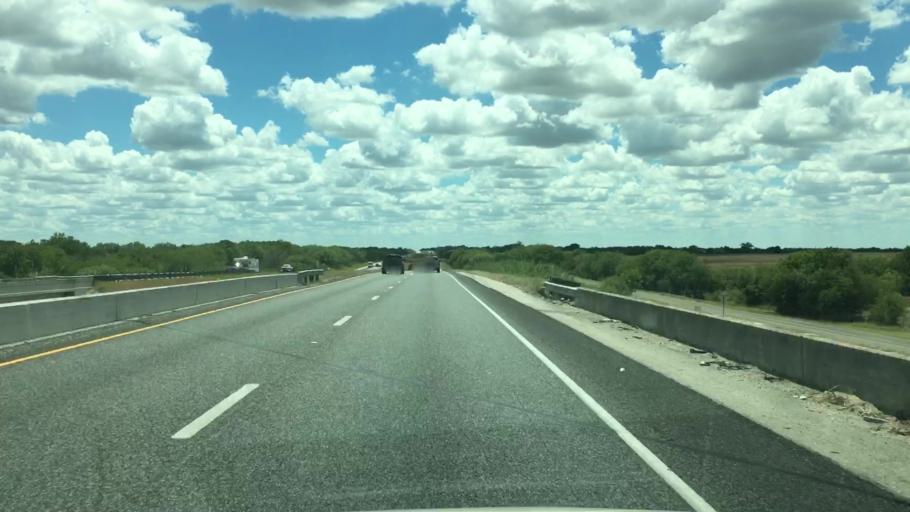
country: US
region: Texas
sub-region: Atascosa County
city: Pleasanton
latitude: 29.0869
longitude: -98.4331
